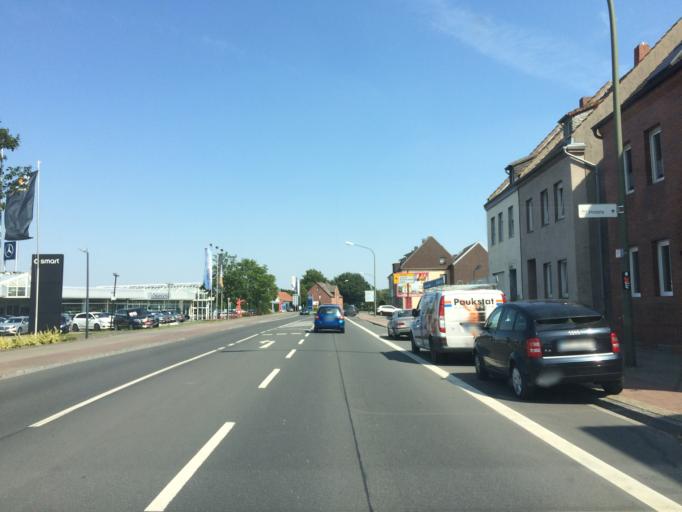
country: DE
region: North Rhine-Westphalia
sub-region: Regierungsbezirk Arnsberg
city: Hamm
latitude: 51.6644
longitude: 7.7650
